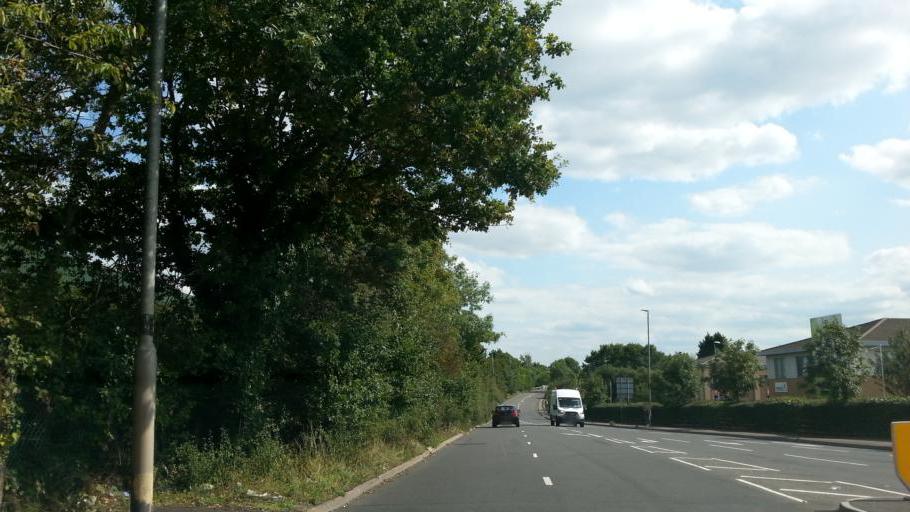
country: GB
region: England
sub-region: Leicestershire
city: Kirby Muxloe
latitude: 52.6303
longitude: -1.2083
